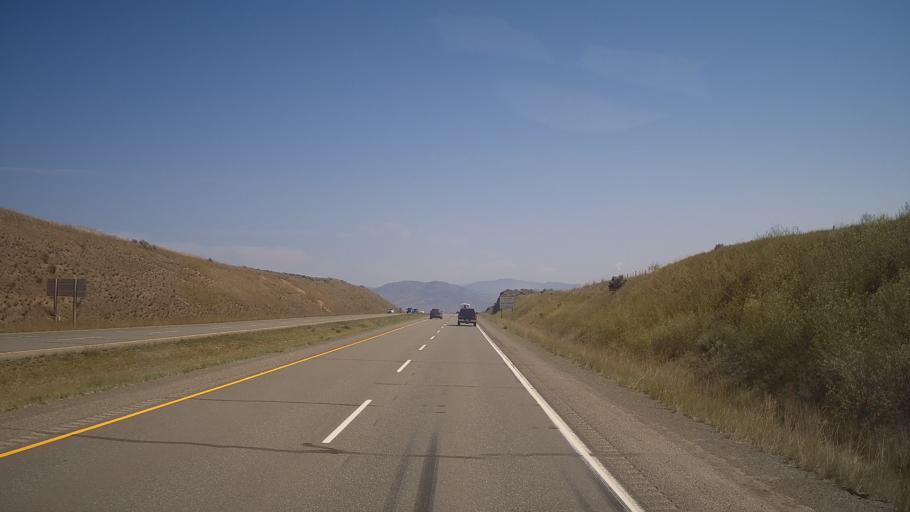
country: CA
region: British Columbia
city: Kamloops
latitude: 50.6572
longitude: -120.4739
